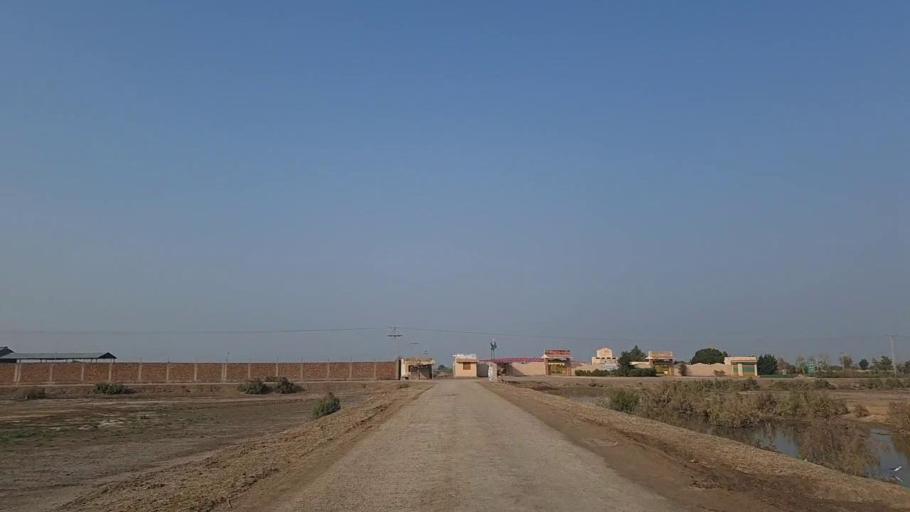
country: PK
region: Sindh
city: Jam Sahib
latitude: 26.2892
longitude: 68.6087
